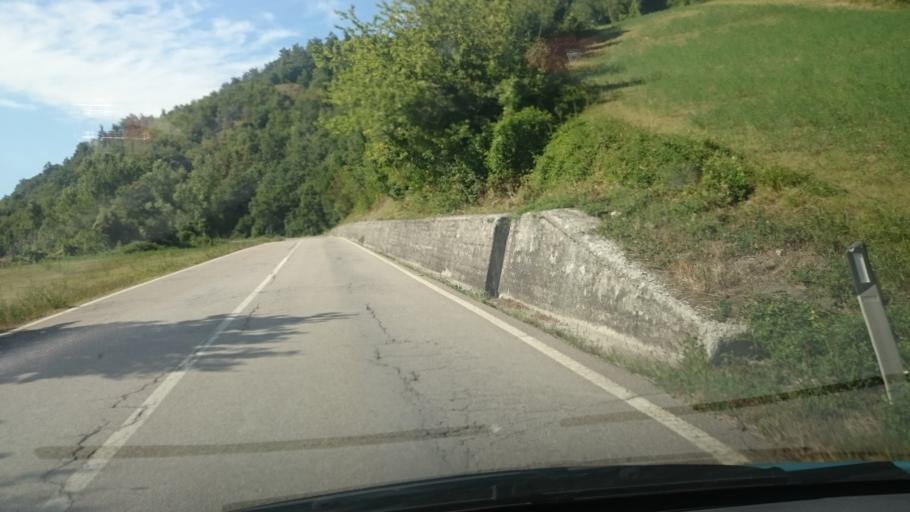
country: IT
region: Emilia-Romagna
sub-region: Provincia di Reggio Emilia
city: Toano
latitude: 44.4091
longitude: 10.6041
